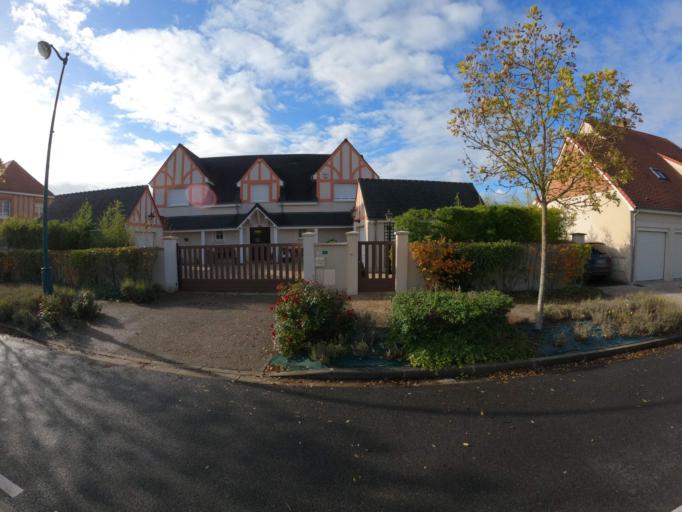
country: FR
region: Ile-de-France
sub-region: Departement de Seine-et-Marne
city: Magny-le-Hongre
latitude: 48.8610
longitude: 2.8238
